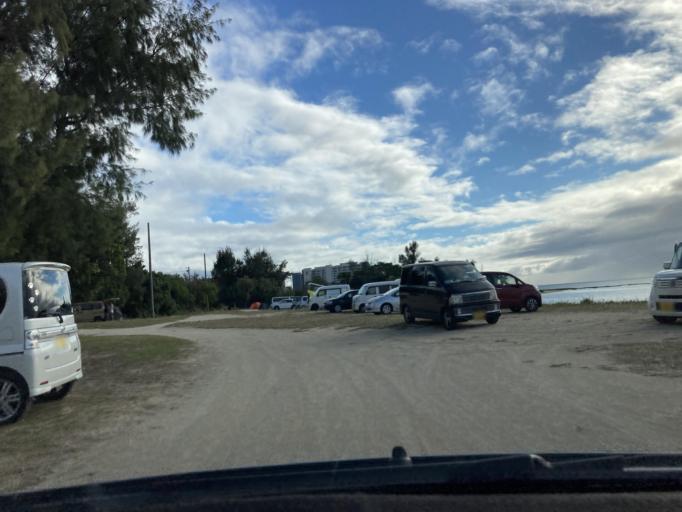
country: JP
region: Okinawa
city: Itoman
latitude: 26.1081
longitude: 127.6617
